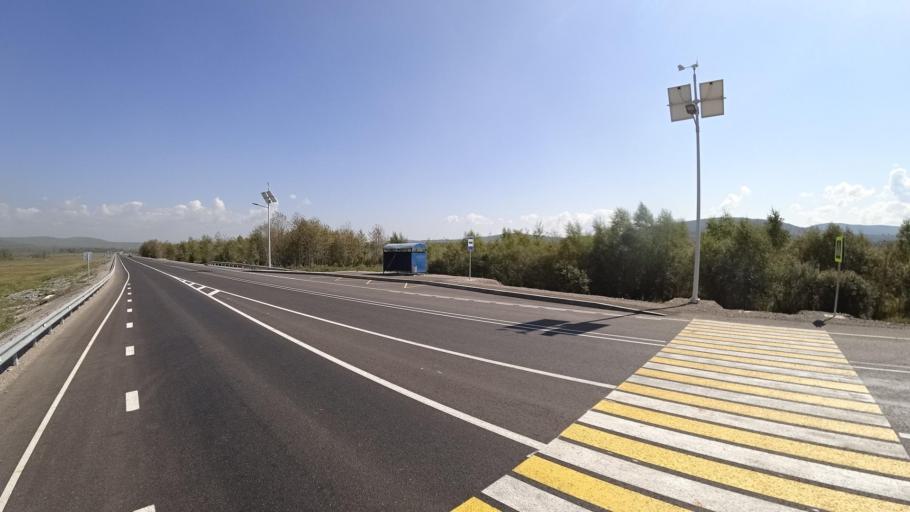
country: RU
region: Jewish Autonomous Oblast
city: Londoko
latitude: 49.0033
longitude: 131.9476
